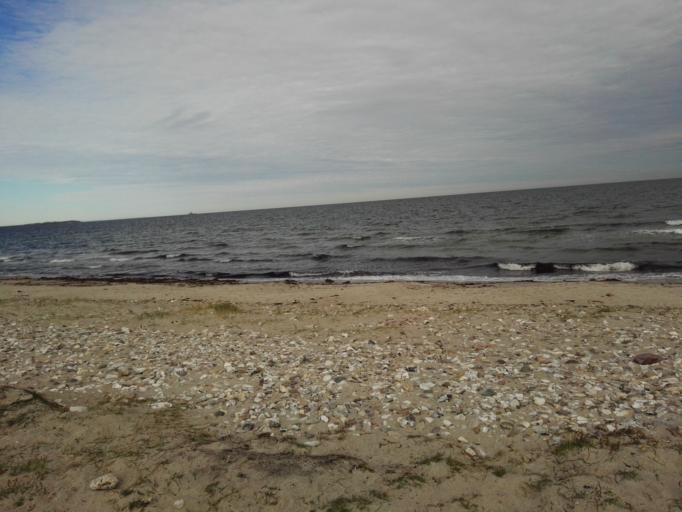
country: DK
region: Zealand
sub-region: Odsherred Kommune
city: Nykobing Sjaelland
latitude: 55.9637
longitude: 11.7377
